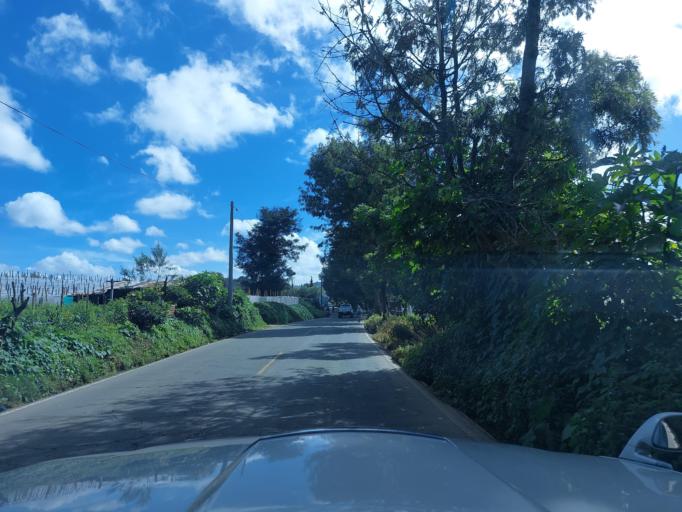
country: GT
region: Chimaltenango
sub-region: Municipio de Zaragoza
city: Zaragoza
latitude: 14.6706
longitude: -90.8996
